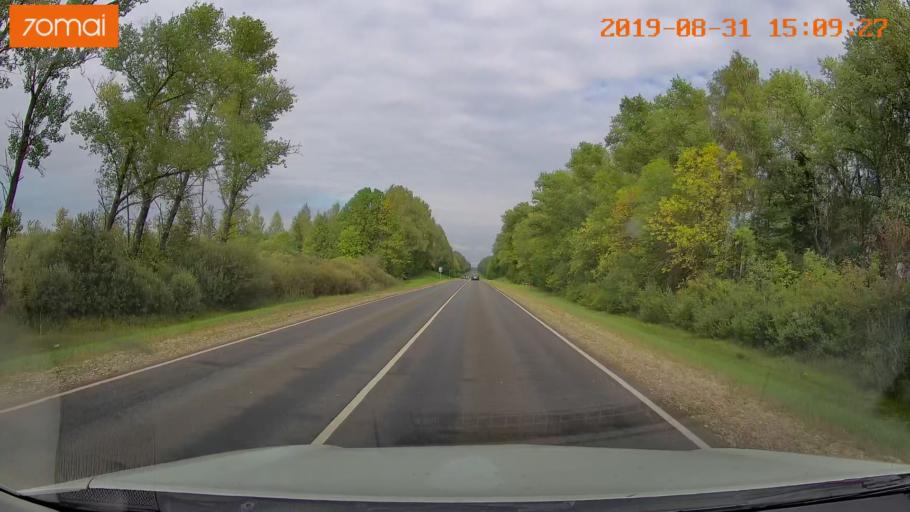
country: RU
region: Kaluga
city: Spas-Demensk
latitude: 54.4021
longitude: 34.2012
